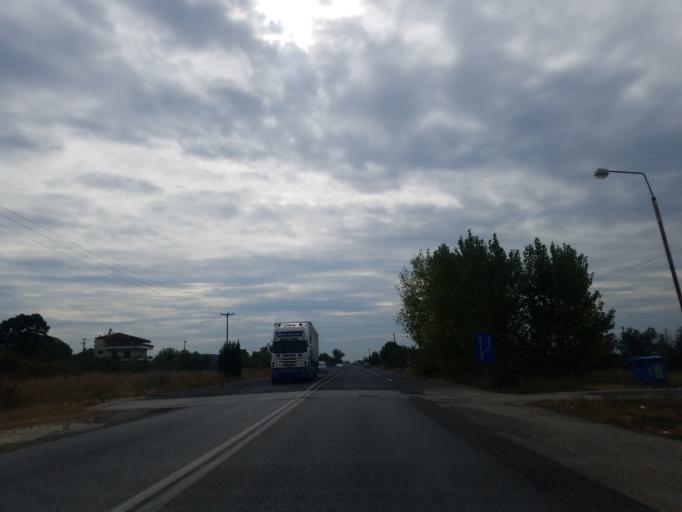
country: GR
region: Thessaly
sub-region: Trikala
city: Kalampaka
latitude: 39.6897
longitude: 21.6463
